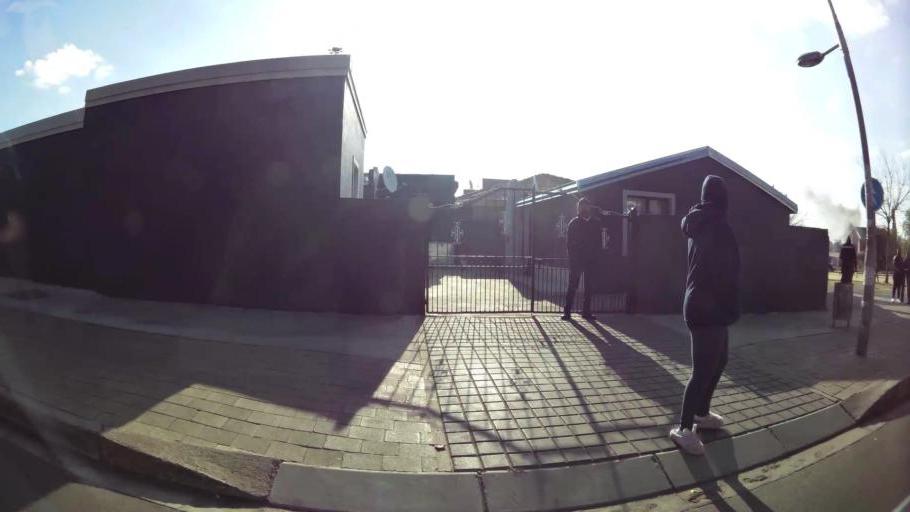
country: ZA
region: Gauteng
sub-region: City of Johannesburg Metropolitan Municipality
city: Soweto
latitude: -26.2575
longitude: 27.9155
